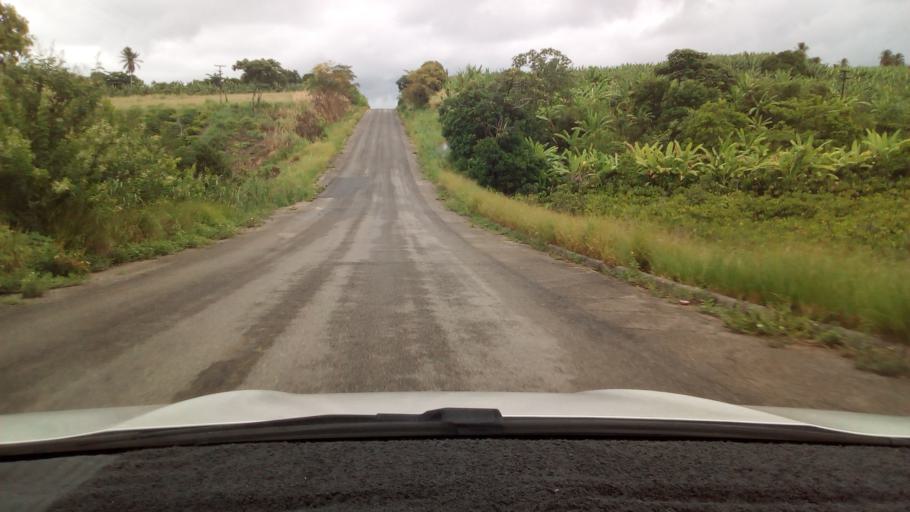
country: BR
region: Paraiba
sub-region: Pitimbu
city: Pitimbu
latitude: -7.3594
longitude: -34.8198
